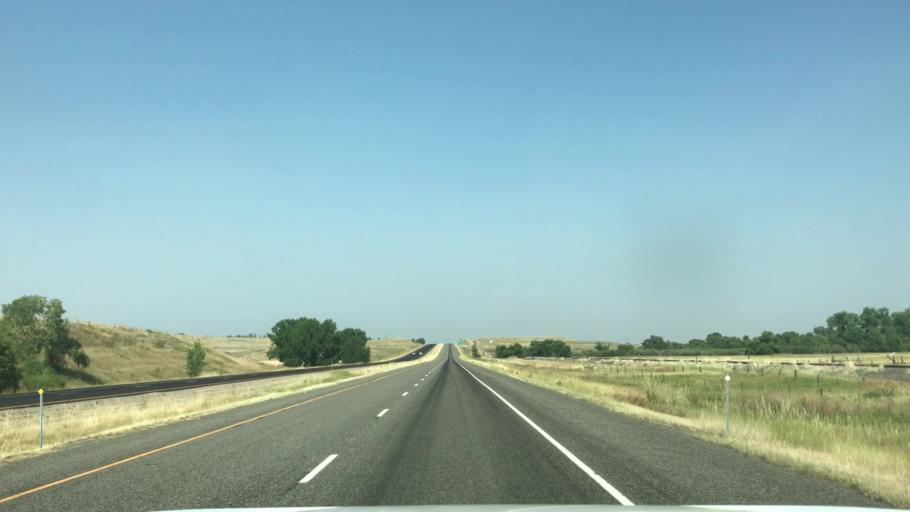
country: US
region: Montana
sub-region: Cascade County
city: Sun Prairie
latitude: 47.2411
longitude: -111.7292
